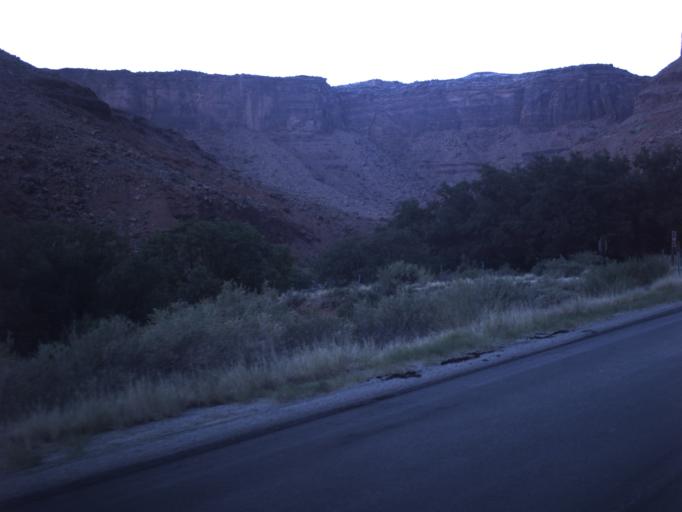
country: US
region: Utah
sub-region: Grand County
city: Moab
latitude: 38.6391
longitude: -109.4784
